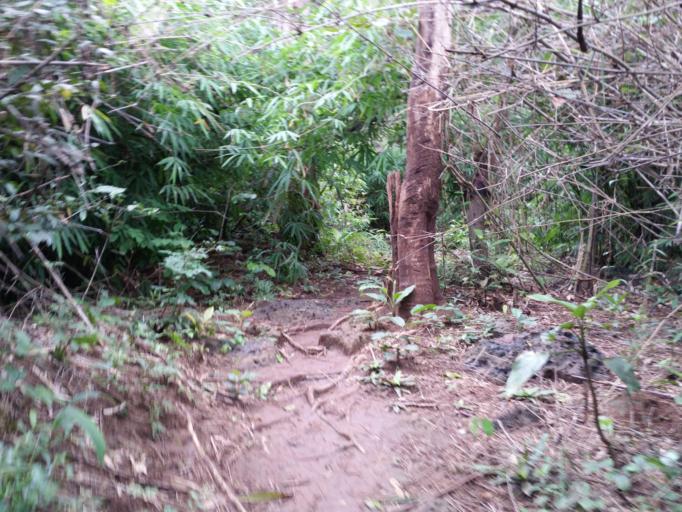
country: LA
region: Xekong
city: Thateng
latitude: 15.5268
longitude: 106.2725
